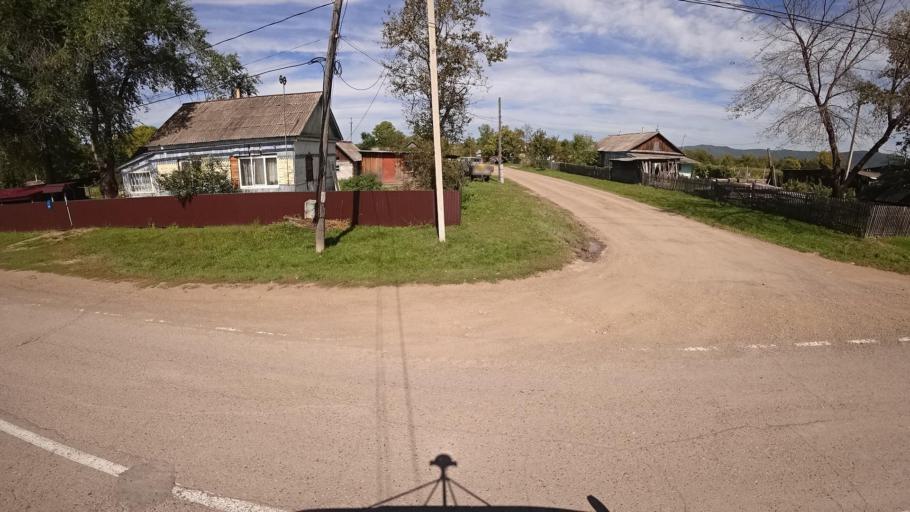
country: RU
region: Primorskiy
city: Yakovlevka
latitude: 44.4299
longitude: 133.5687
